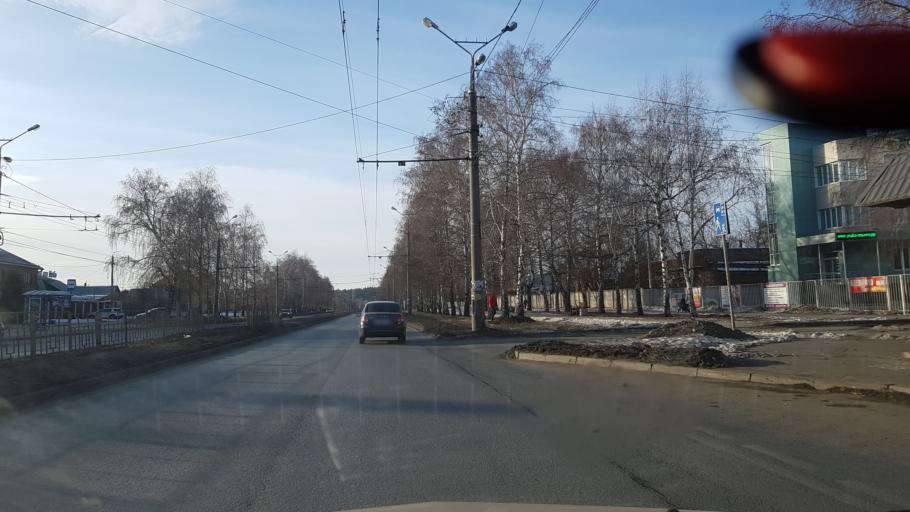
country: RU
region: Samara
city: Tol'yatti
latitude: 53.5305
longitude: 49.4110
